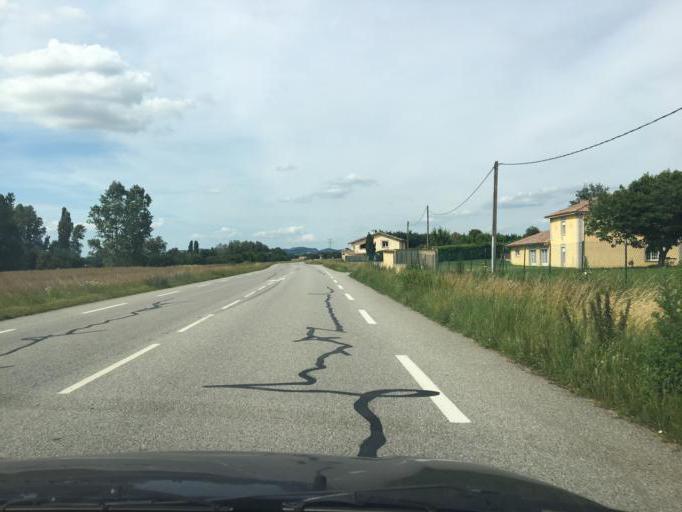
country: FR
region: Rhone-Alpes
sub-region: Departement de la Drome
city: Chanos-Curson
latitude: 45.0683
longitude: 4.9330
